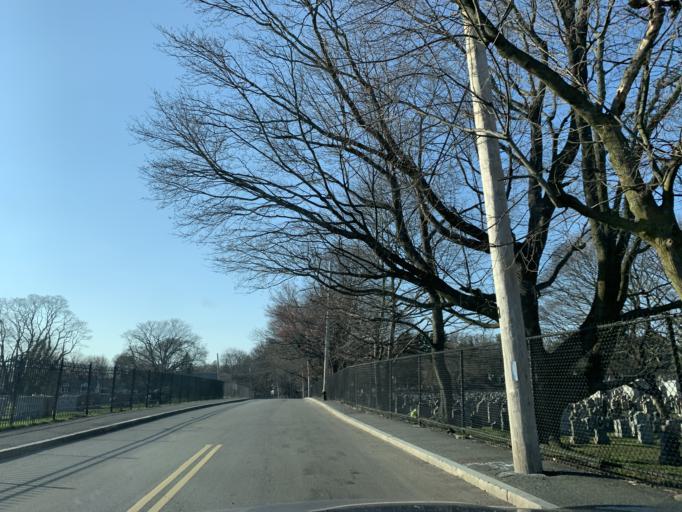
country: US
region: Massachusetts
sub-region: Suffolk County
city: Jamaica Plain
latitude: 42.2874
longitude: -71.1107
